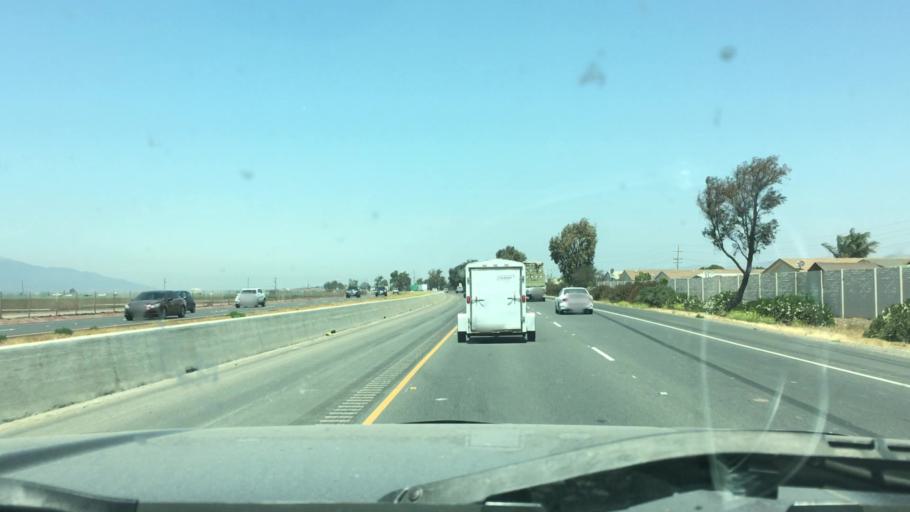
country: US
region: California
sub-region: Monterey County
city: Soledad
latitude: 36.4212
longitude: -121.3252
